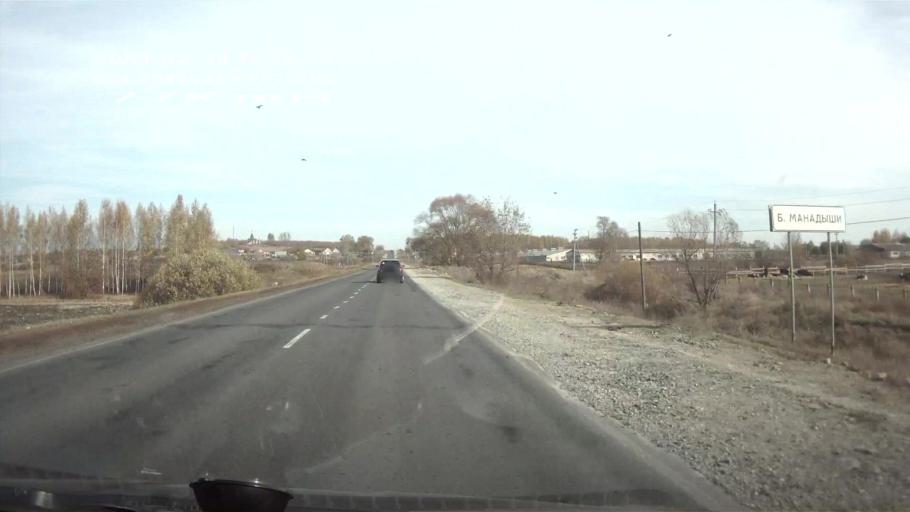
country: RU
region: Mordoviya
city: Atyashevo
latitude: 54.5590
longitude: 45.9733
